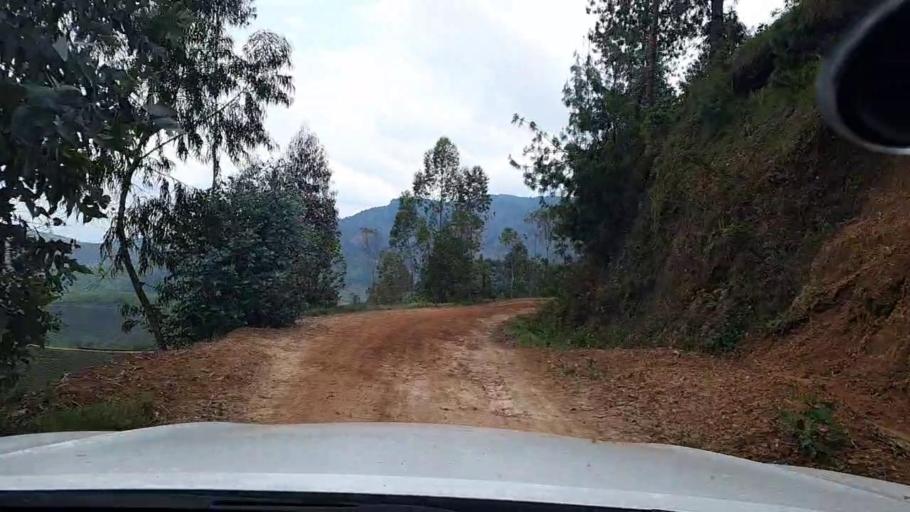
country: RW
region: Western Province
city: Kibuye
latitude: -2.1651
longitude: 29.4534
